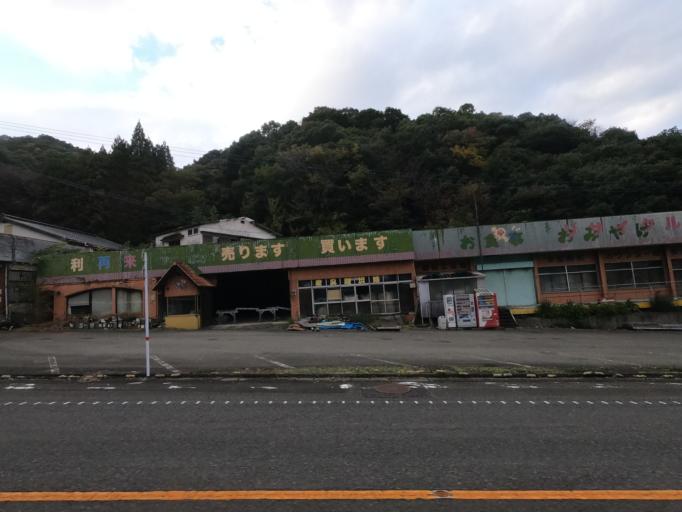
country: JP
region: Kumamoto
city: Minamata
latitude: 32.2479
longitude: 130.5003
